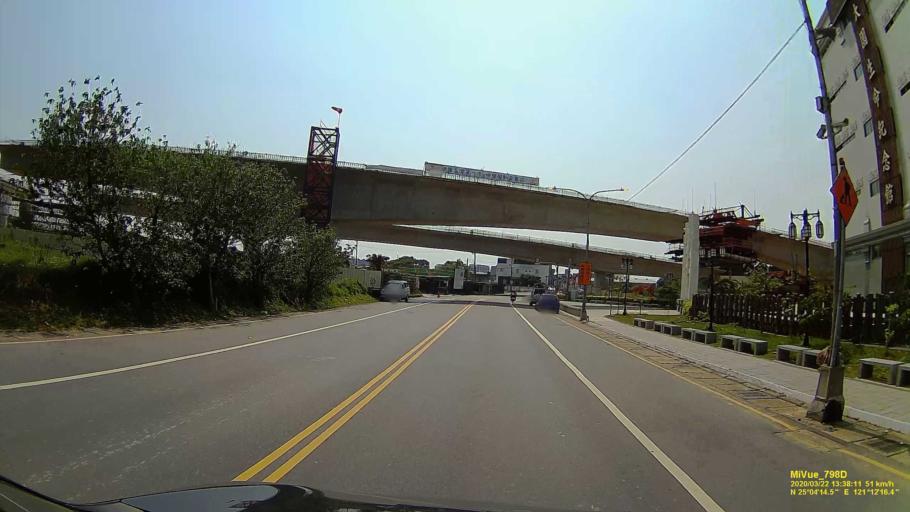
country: TW
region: Taiwan
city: Taoyuan City
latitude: 25.0705
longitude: 121.2044
